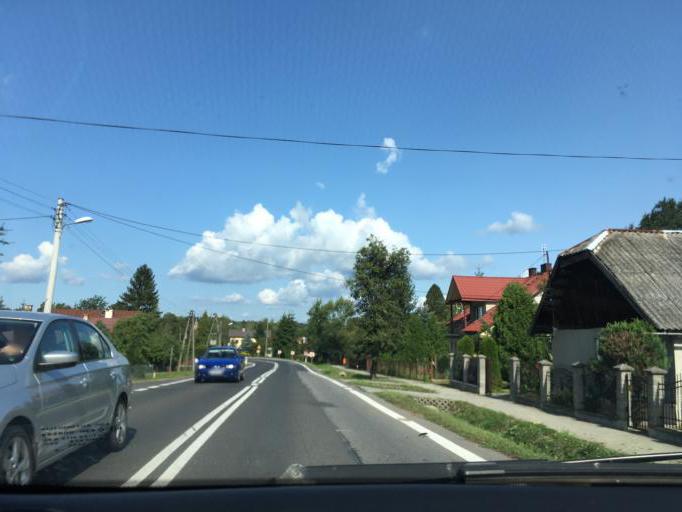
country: PL
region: Subcarpathian Voivodeship
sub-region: Powiat leski
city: Olszanica
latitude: 49.4741
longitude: 22.4536
